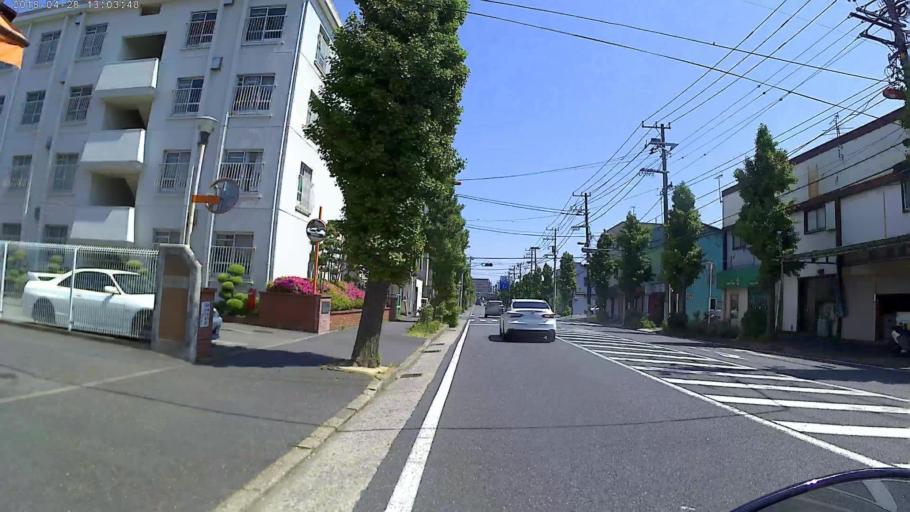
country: JP
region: Kanagawa
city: Yokosuka
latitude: 35.2503
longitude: 139.6799
